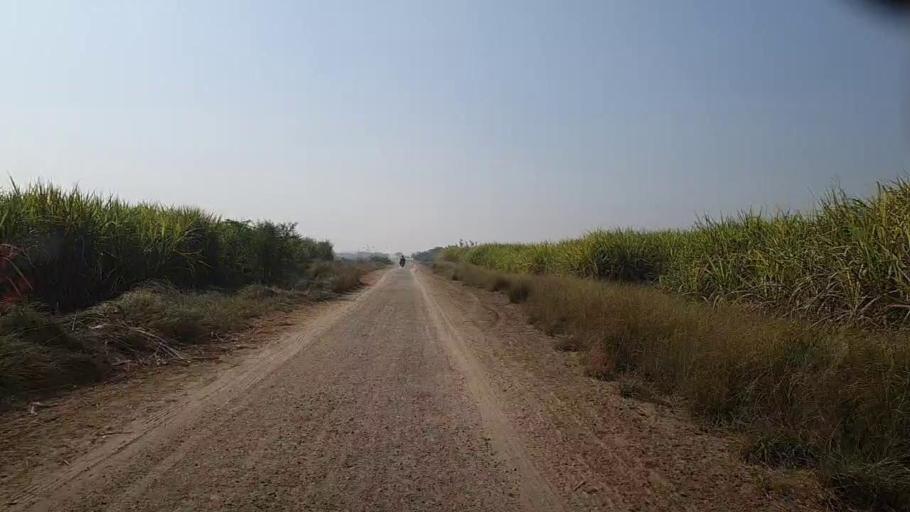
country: PK
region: Sindh
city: Bozdar
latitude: 27.2602
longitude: 68.6187
